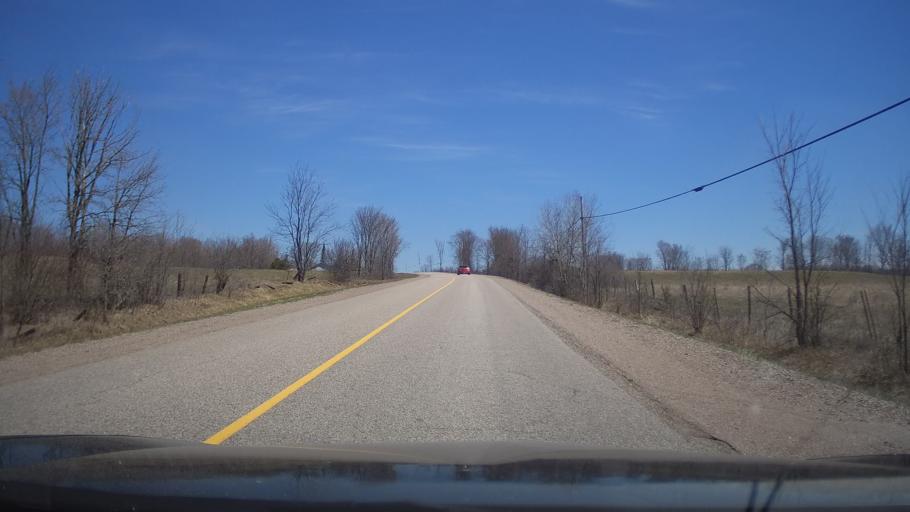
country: CA
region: Ontario
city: Arnprior
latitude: 45.5336
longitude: -76.3705
